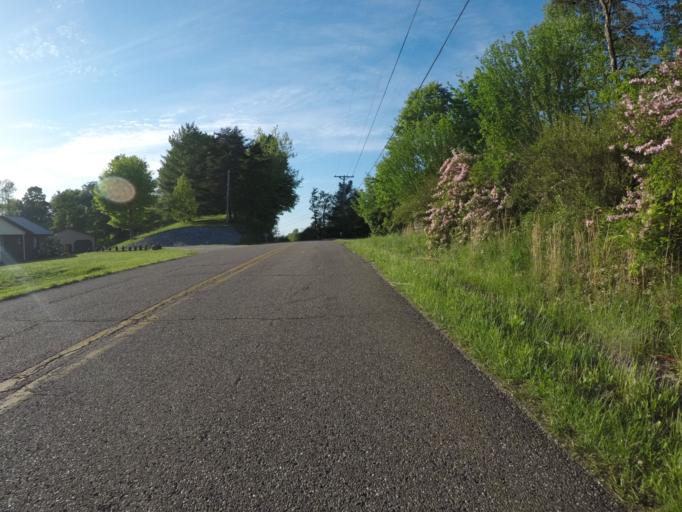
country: US
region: West Virginia
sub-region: Cabell County
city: Huntington
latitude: 38.5154
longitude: -82.4248
